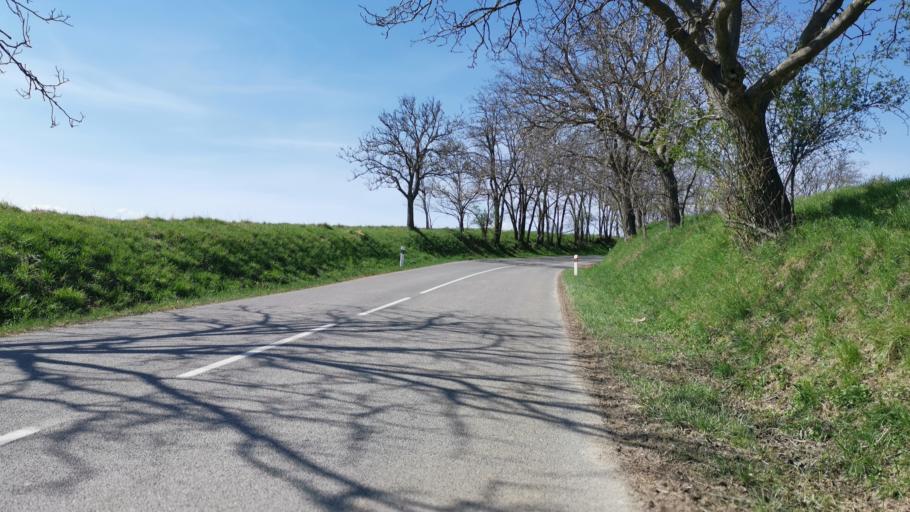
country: SK
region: Trnavsky
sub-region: Okres Skalica
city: Holic
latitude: 48.7382
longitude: 17.2058
